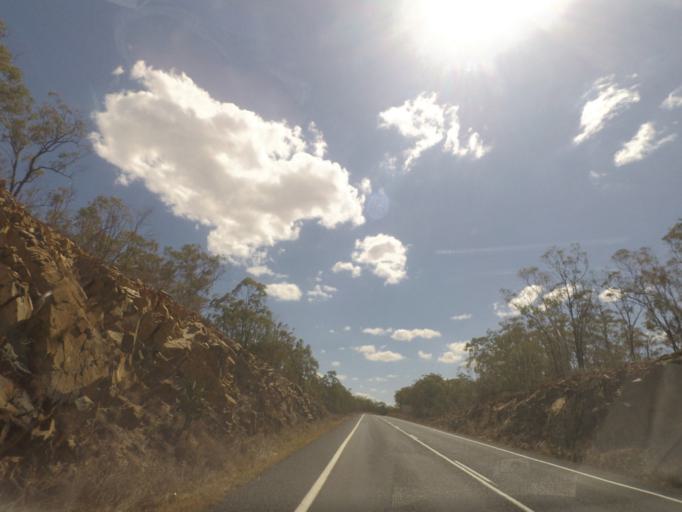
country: AU
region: Queensland
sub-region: Southern Downs
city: Warwick
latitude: -28.1622
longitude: 151.6839
